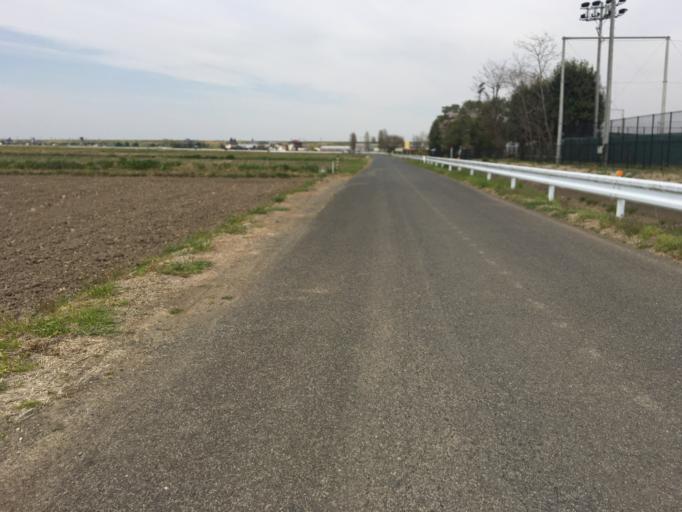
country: JP
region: Saitama
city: Shiki
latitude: 35.8590
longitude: 139.5738
